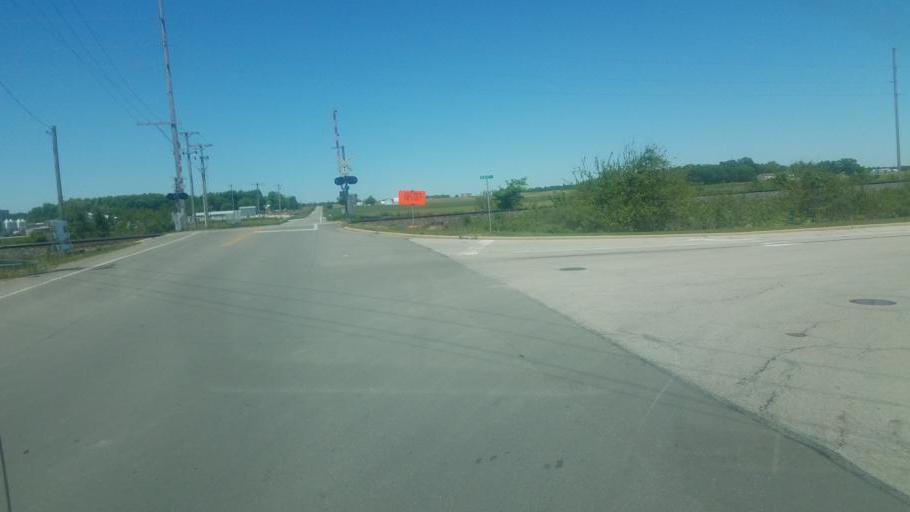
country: US
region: Ohio
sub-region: Darke County
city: Versailles
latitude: 40.2259
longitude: -84.4651
